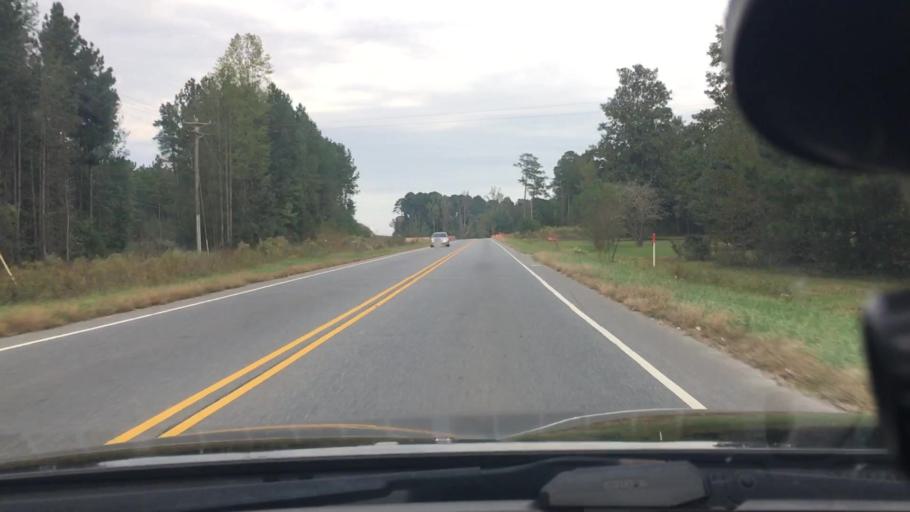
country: US
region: North Carolina
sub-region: Montgomery County
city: Troy
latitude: 35.3271
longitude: -79.9370
